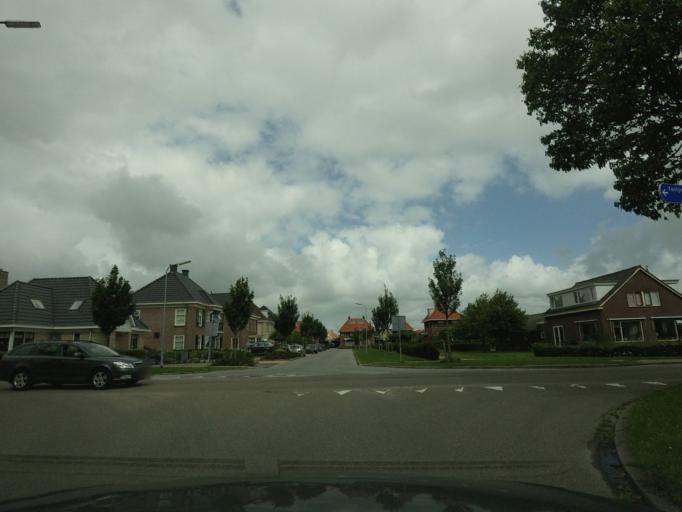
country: NL
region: North Holland
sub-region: Gemeente Schagen
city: Harenkarspel
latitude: 52.7337
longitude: 4.7562
